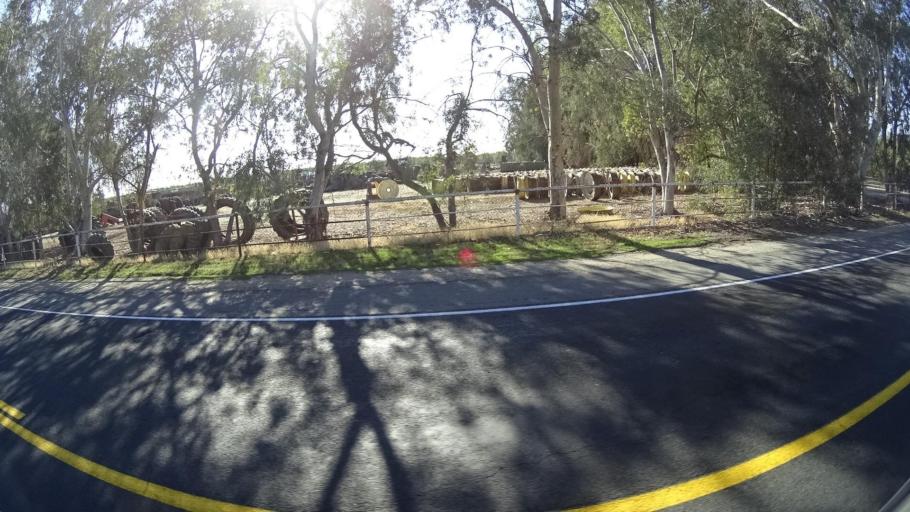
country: US
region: California
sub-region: Kern County
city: Delano
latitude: 35.7177
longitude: -119.3204
